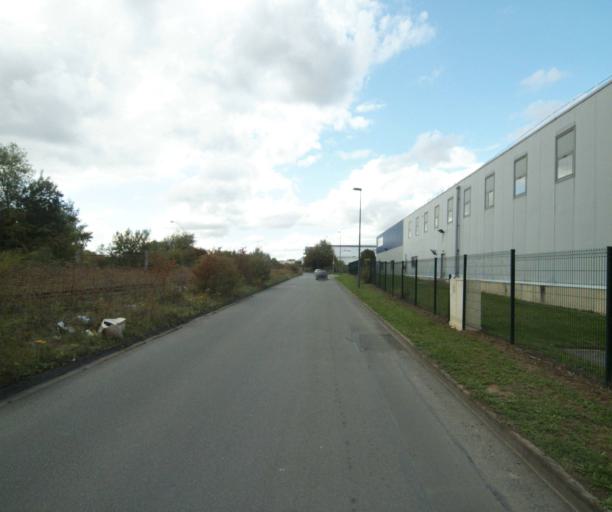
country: FR
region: Nord-Pas-de-Calais
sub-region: Departement du Nord
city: Lomme
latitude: 50.6367
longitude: 2.9831
